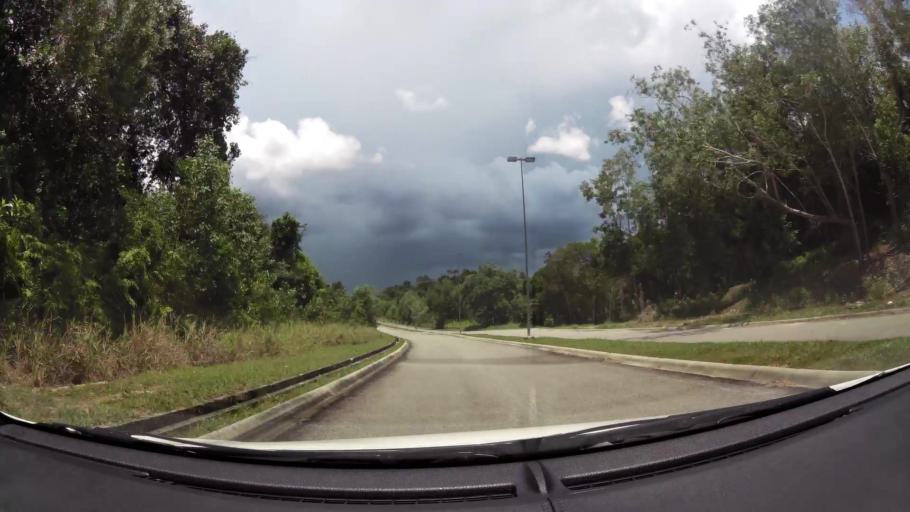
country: BN
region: Brunei and Muara
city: Bandar Seri Begawan
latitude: 4.9492
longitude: 114.8932
